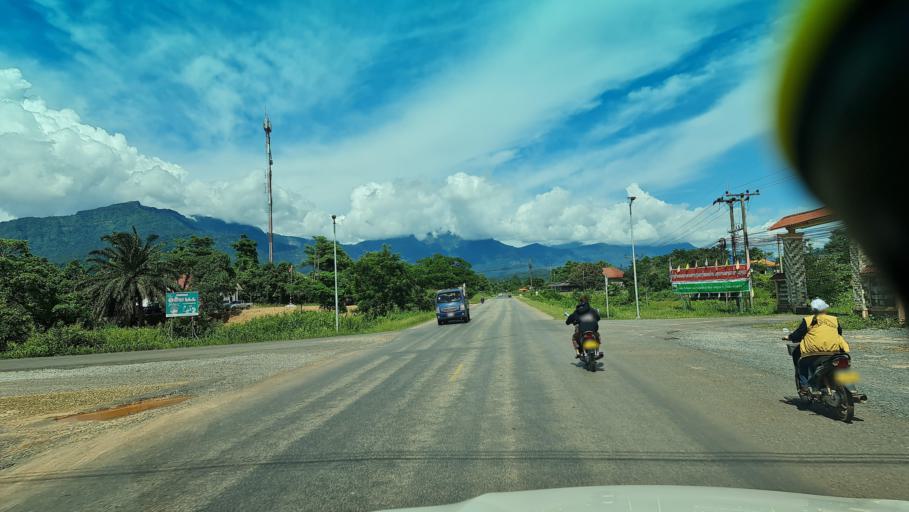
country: LA
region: Bolikhamxai
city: Ban Nahin
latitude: 18.3004
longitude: 104.1189
